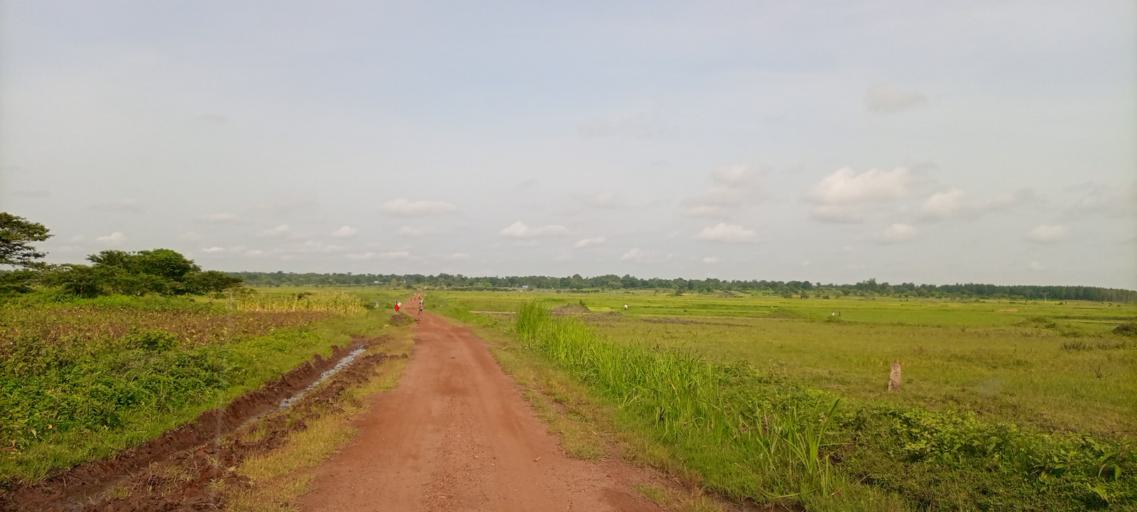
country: UG
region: Eastern Region
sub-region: Kibuku District
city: Kibuku
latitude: 1.1018
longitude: 33.7778
